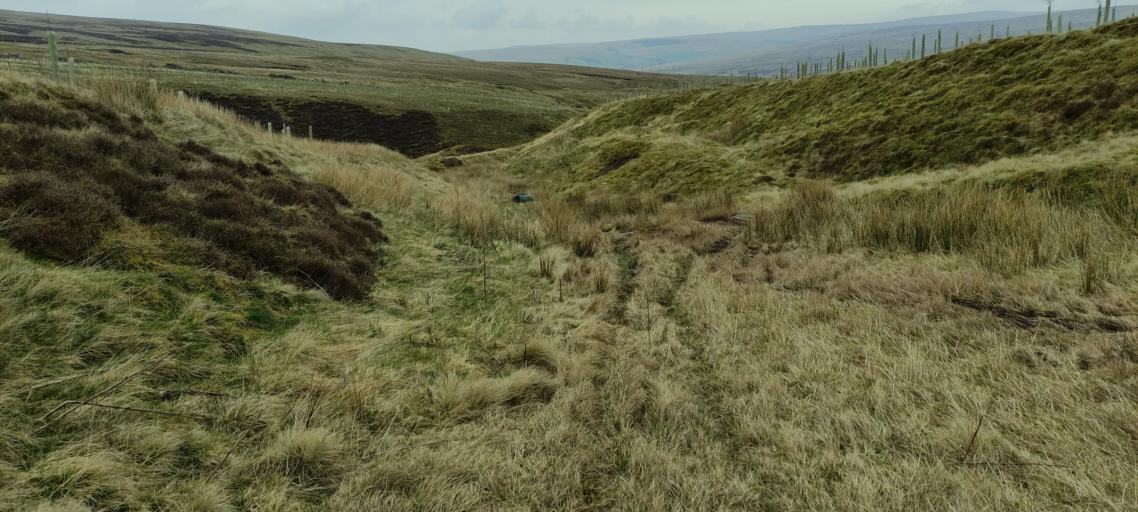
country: GB
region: England
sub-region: Northumberland
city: Greenhead
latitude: 54.7723
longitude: -2.5336
